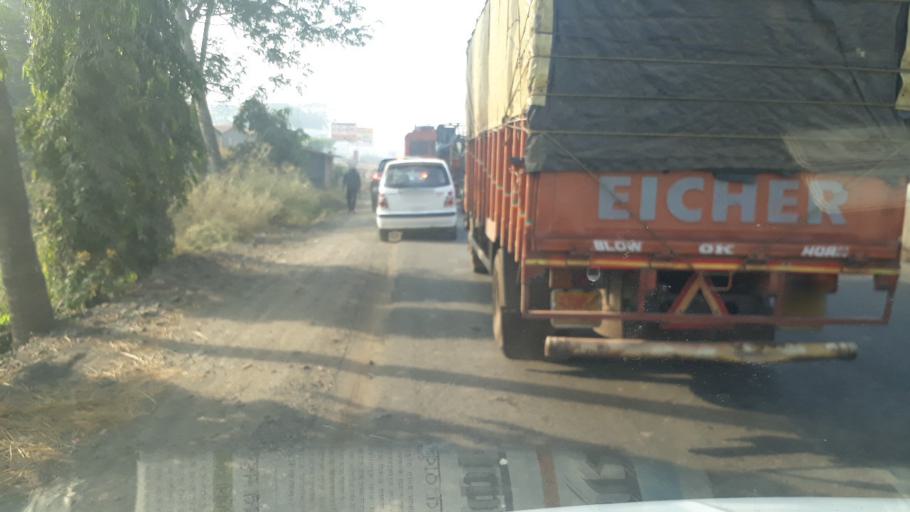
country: IN
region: Maharashtra
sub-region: Raigarh
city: Kalundri
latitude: 18.9247
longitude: 73.1261
